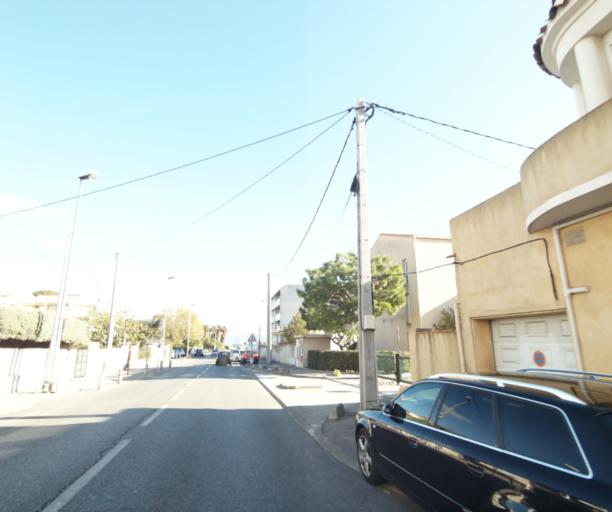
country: FR
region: Provence-Alpes-Cote d'Azur
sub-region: Departement des Bouches-du-Rhone
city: La Ciotat
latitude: 43.1829
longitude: 5.6135
